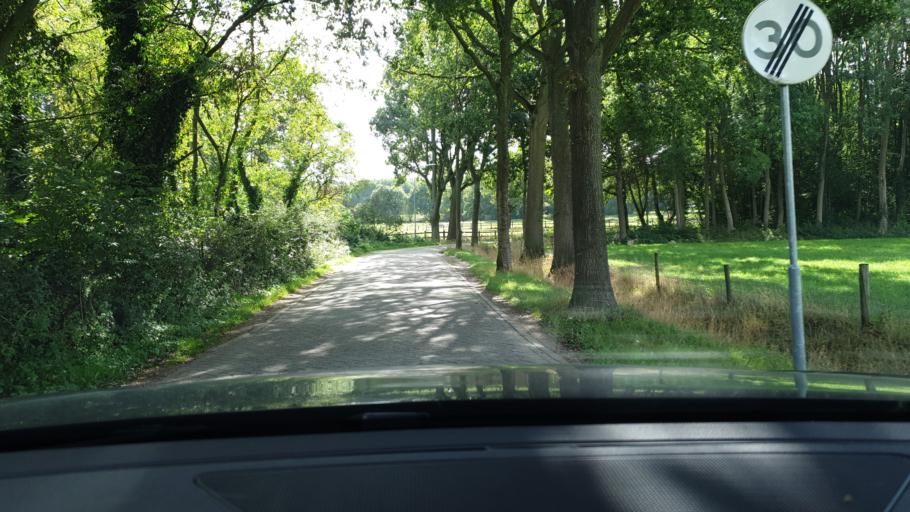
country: NL
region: Gelderland
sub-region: Gemeente Groesbeek
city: De Horst
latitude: 51.7779
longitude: 5.9822
